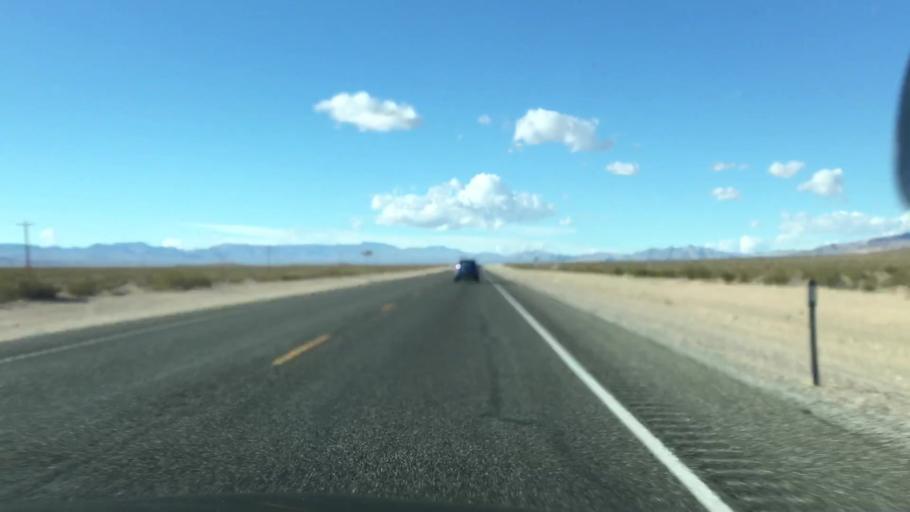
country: US
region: Nevada
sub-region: Nye County
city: Beatty
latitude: 36.7237
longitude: -116.6212
